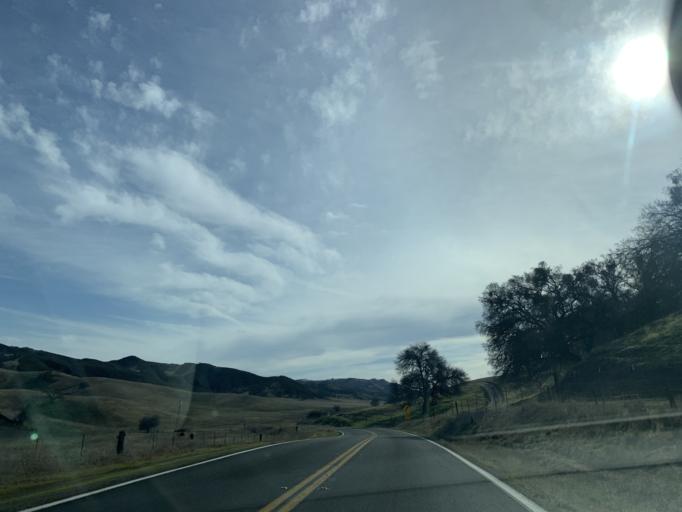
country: US
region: California
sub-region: Monterey County
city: Greenfield
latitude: 36.5028
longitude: -121.0888
